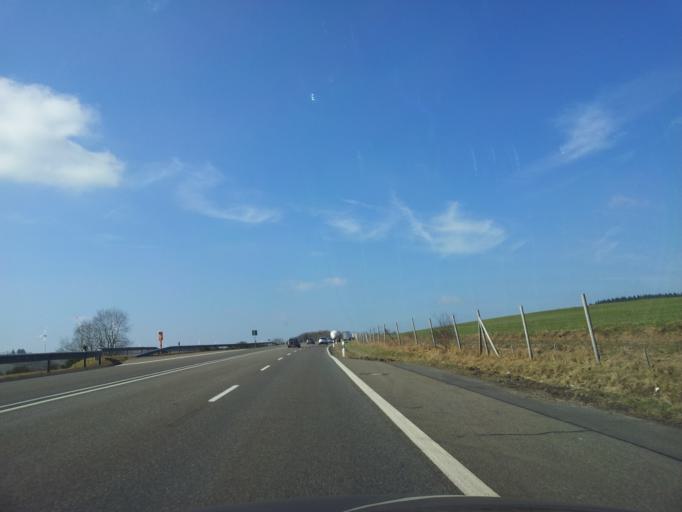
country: DE
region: Rheinland-Pfalz
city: Habscheid
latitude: 50.1981
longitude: 6.2710
